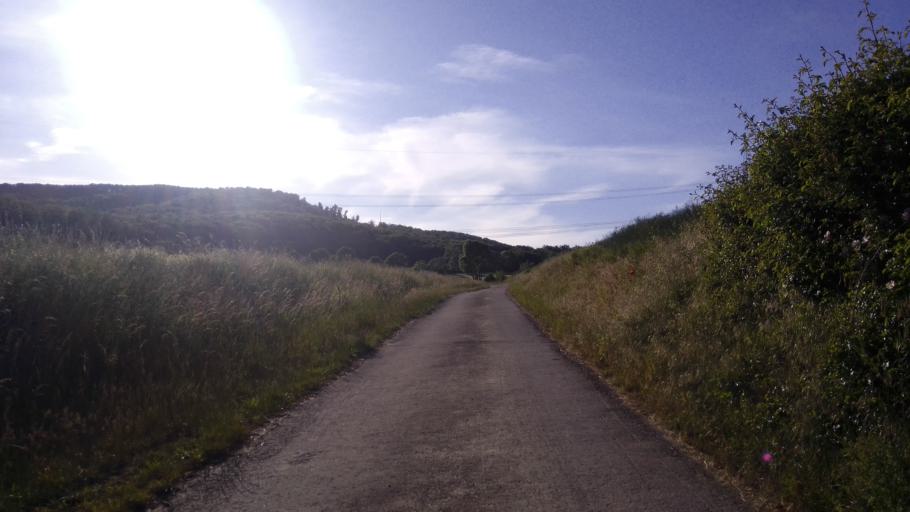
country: DE
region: Lower Saxony
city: Salzhemmendorf
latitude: 52.0337
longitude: 9.5966
